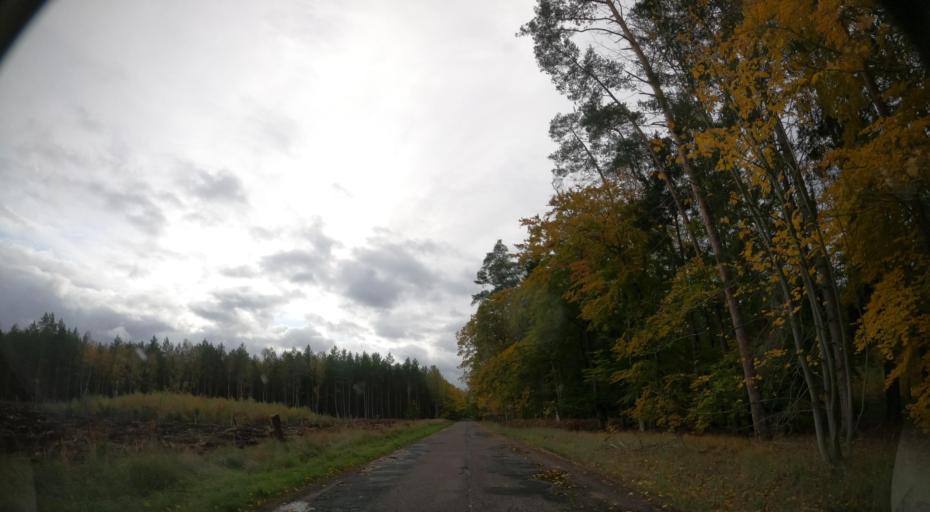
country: PL
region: West Pomeranian Voivodeship
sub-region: Powiat goleniowski
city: Stepnica
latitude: 53.6835
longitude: 14.6756
